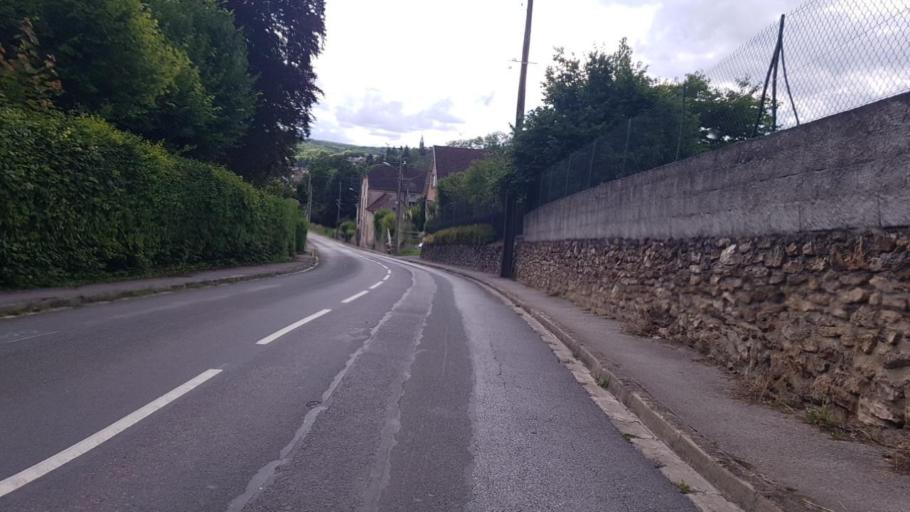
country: FR
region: Picardie
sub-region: Departement de l'Aisne
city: Crezancy
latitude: 49.0760
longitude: 3.5000
